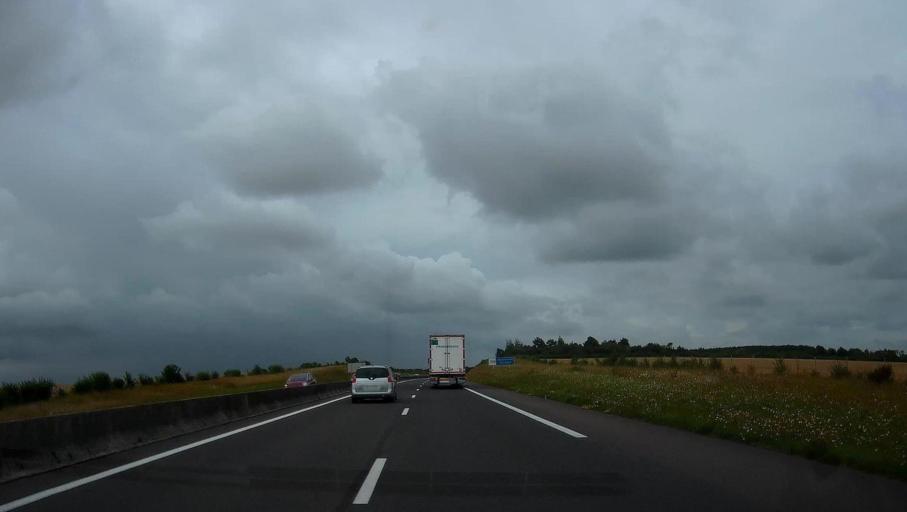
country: FR
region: Champagne-Ardenne
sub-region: Departement de l'Aube
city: Mailly-le-Camp
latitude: 48.7061
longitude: 4.2077
